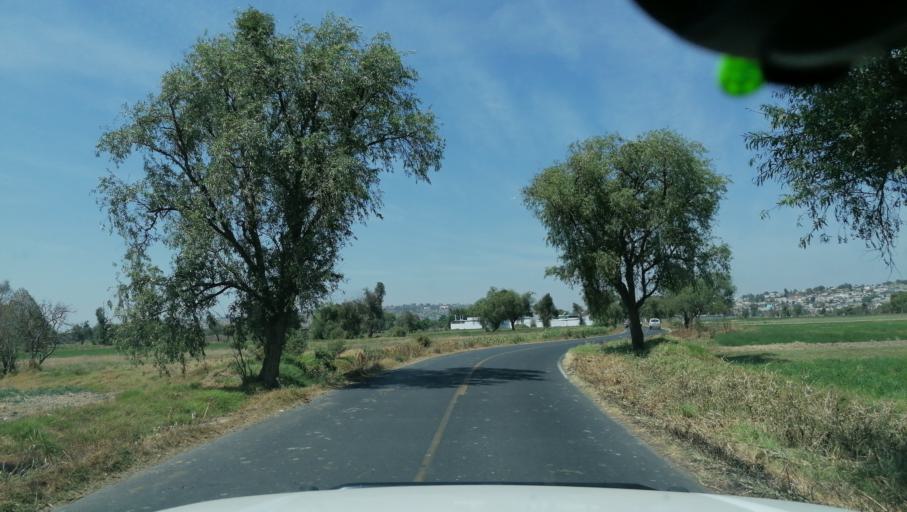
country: MX
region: Tlaxcala
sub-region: Tetlatlahuca
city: Tetlatlahuca
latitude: 19.2210
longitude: -98.2921
